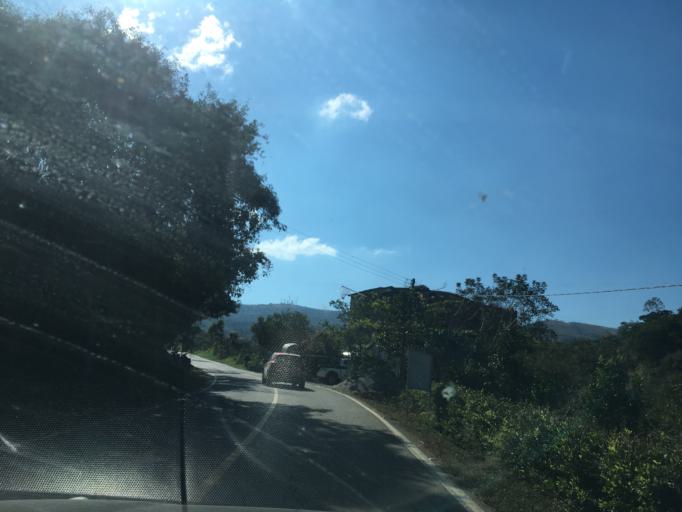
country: CO
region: Santander
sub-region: San Gil
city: San Gil
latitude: 6.5992
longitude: -73.1560
